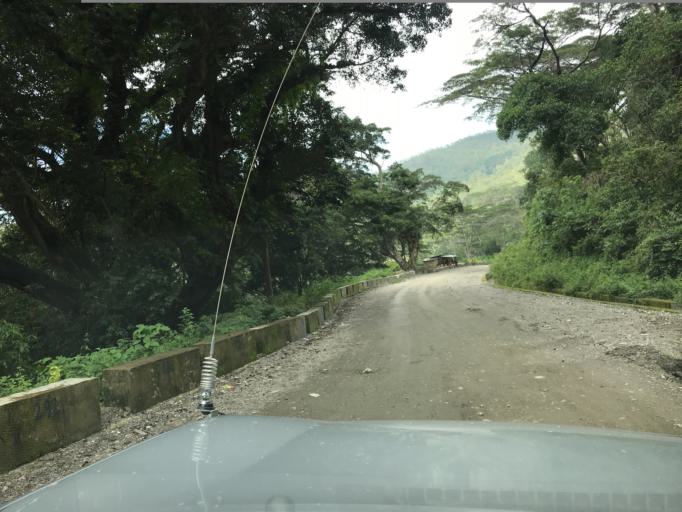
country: TL
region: Aileu
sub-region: Aileu Villa
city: Aileu
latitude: -8.6719
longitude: 125.5525
